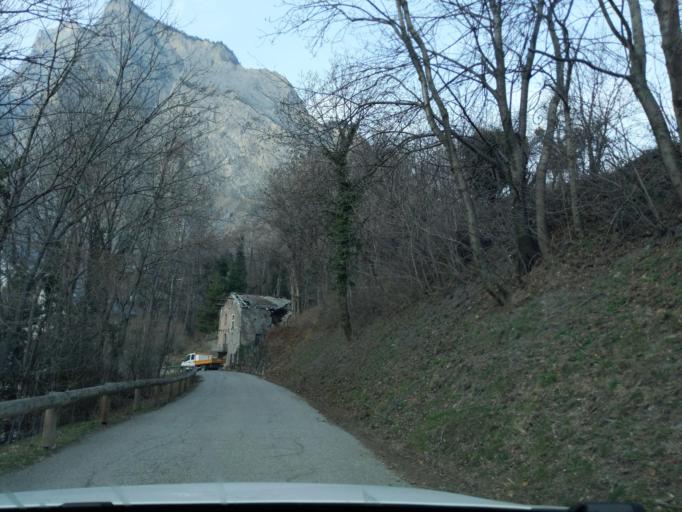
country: FR
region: Rhone-Alpes
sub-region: Departement de la Savoie
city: Saint-Michel-de-Maurienne
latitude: 45.2378
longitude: 6.4432
